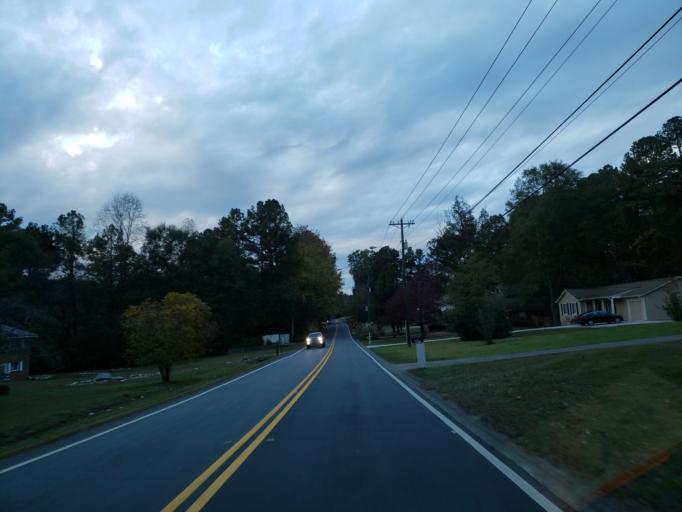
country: US
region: Georgia
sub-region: Cobb County
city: Acworth
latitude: 34.0301
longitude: -84.6856
